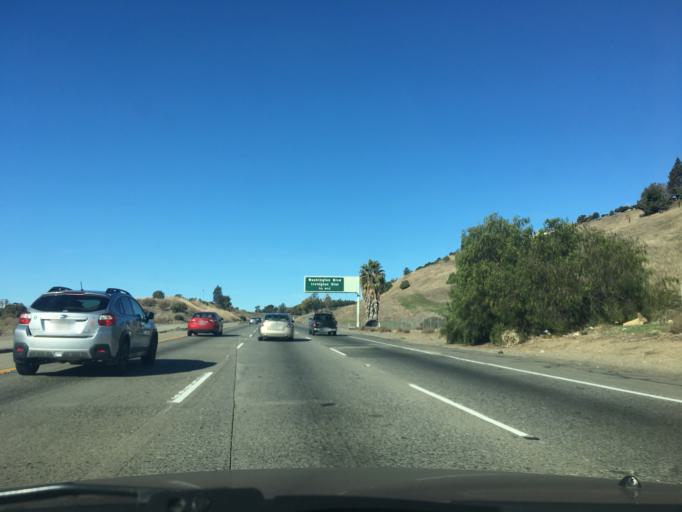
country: US
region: California
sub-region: Alameda County
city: Fremont
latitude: 37.5204
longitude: -121.9432
